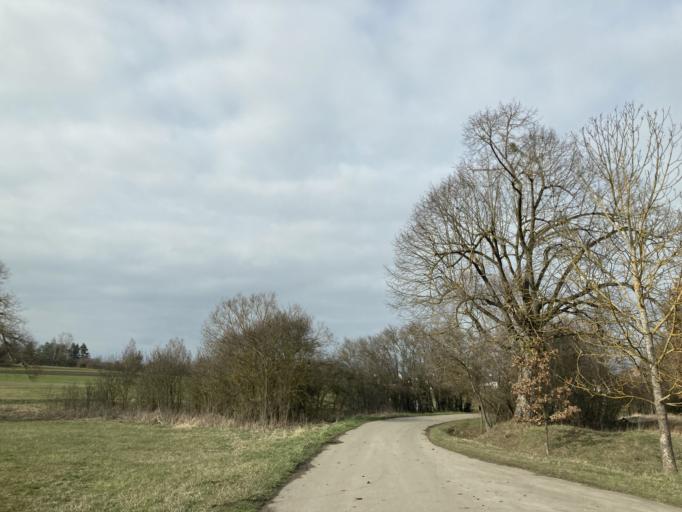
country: DE
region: Baden-Wuerttemberg
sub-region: Tuebingen Region
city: Rottenburg
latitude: 48.4438
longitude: 8.9159
